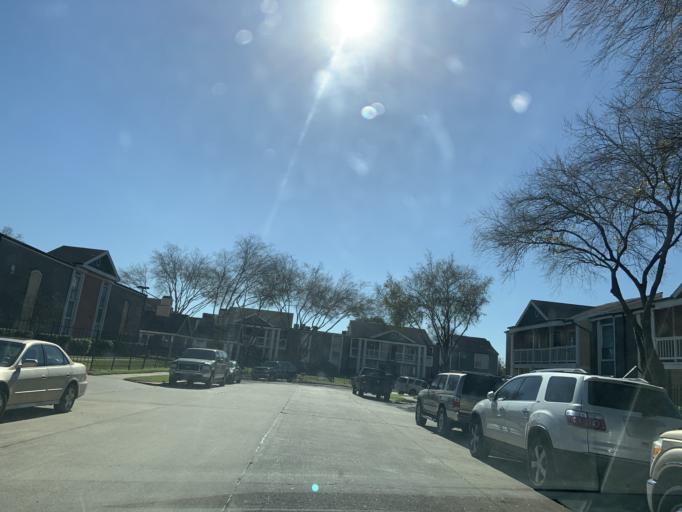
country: US
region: Texas
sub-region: Harris County
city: Bellaire
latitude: 29.6792
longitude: -95.5058
